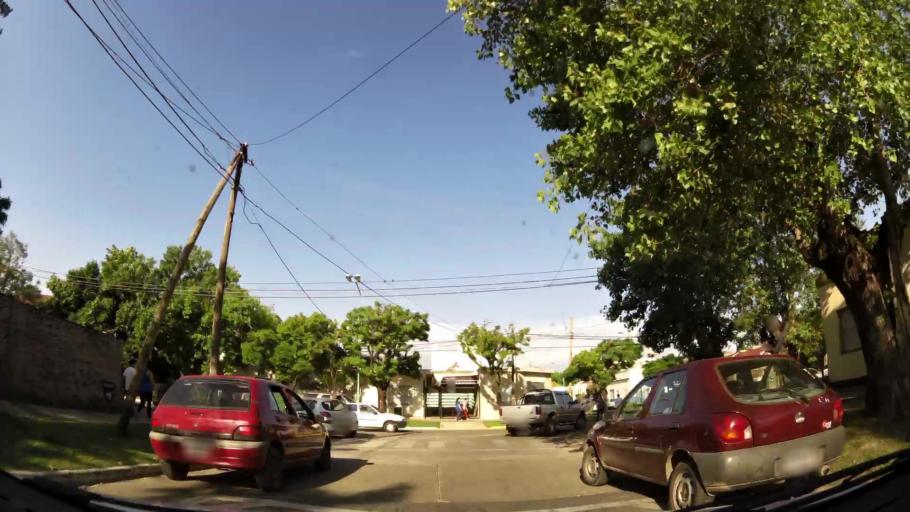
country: AR
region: Buenos Aires
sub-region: Partido de Merlo
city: Merlo
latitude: -34.6688
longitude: -58.7346
